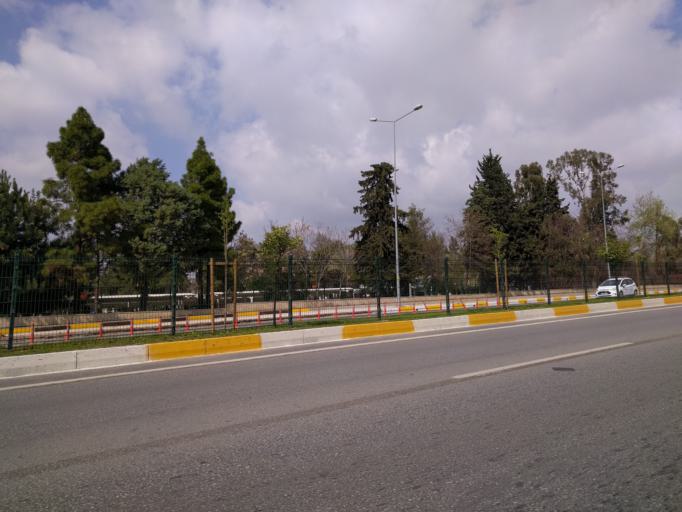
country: TR
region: Antalya
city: Antalya
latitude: 36.9027
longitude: 30.6708
